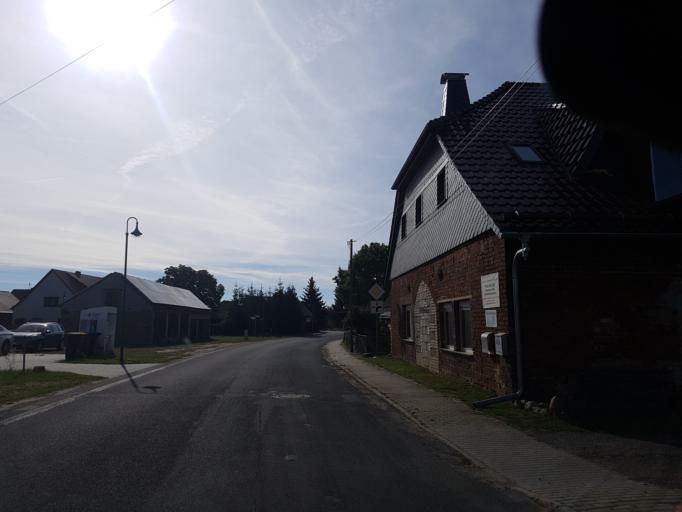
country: DE
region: Brandenburg
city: Schlieben
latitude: 51.7789
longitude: 13.3224
